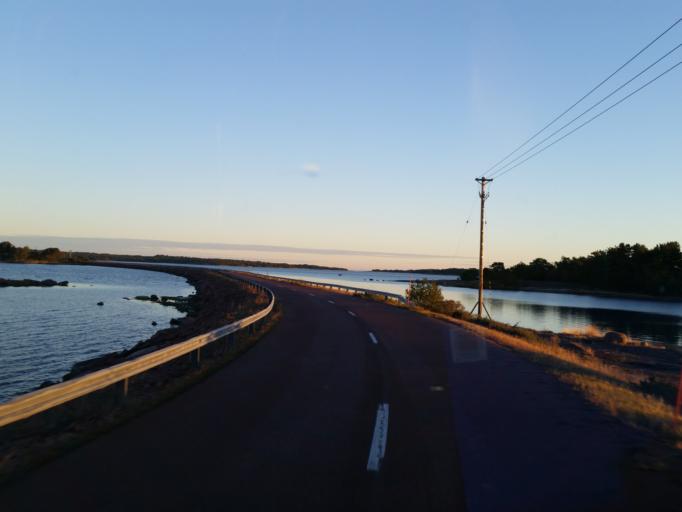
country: AX
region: Alands skaergard
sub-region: Vardoe
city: Vardoe
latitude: 60.3150
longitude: 20.3754
